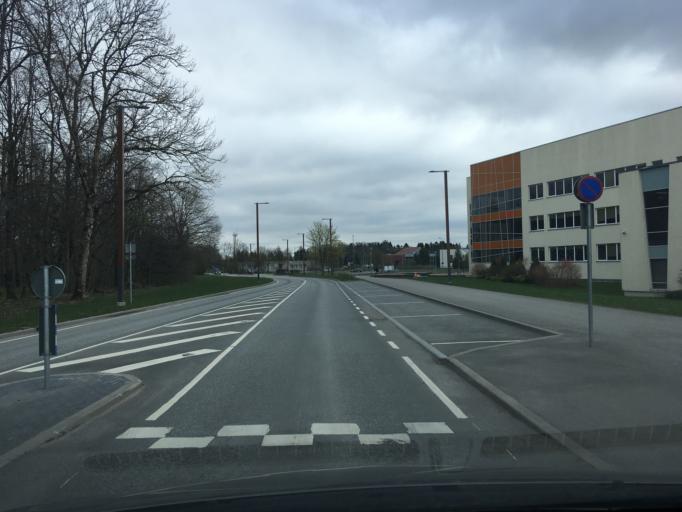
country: EE
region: Harju
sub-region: Rae vald
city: Jueri
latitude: 59.3552
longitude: 24.9071
